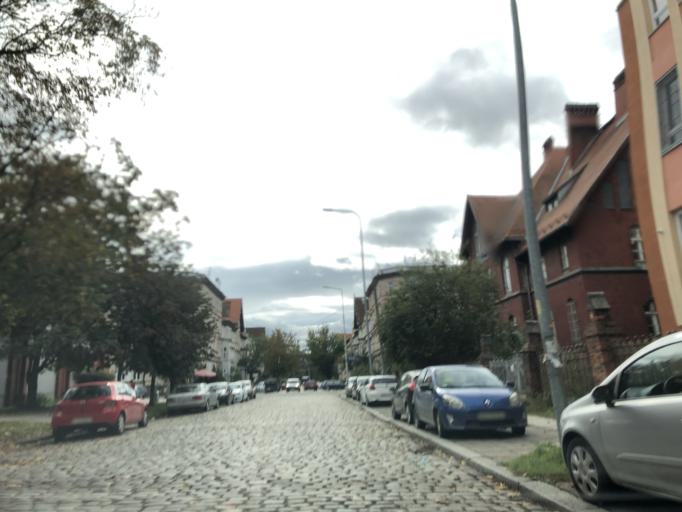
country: PL
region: Lower Silesian Voivodeship
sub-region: Powiat wroclawski
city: Wroclaw
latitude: 51.1292
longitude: 17.0329
